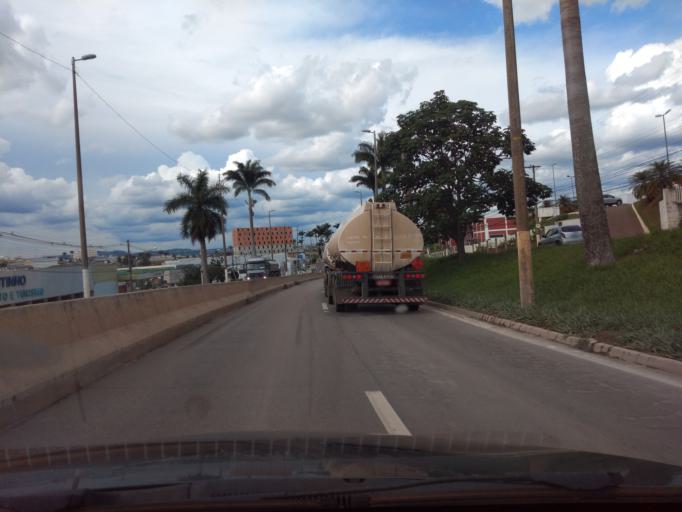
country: BR
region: Minas Gerais
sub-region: Varginha
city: Varginha
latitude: -21.5938
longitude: -45.4393
